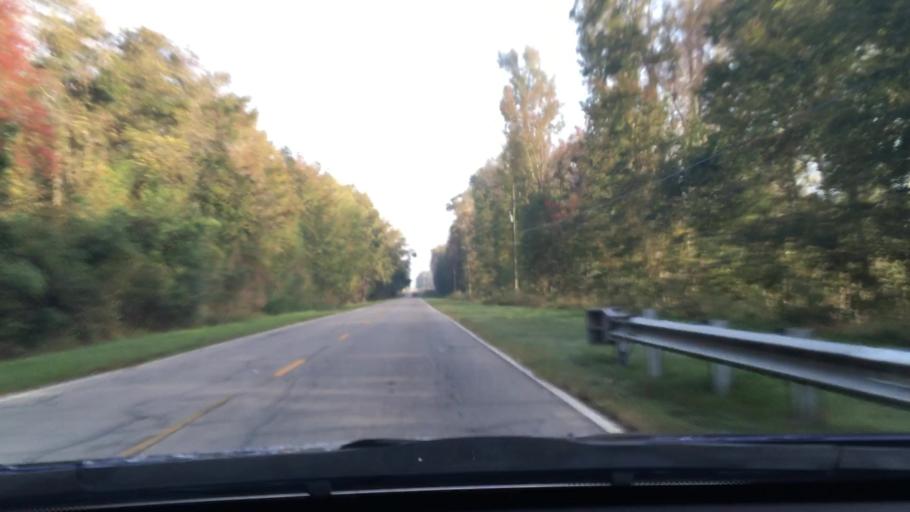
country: US
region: South Carolina
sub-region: Sumter County
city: East Sumter
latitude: 33.9649
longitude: -80.3015
